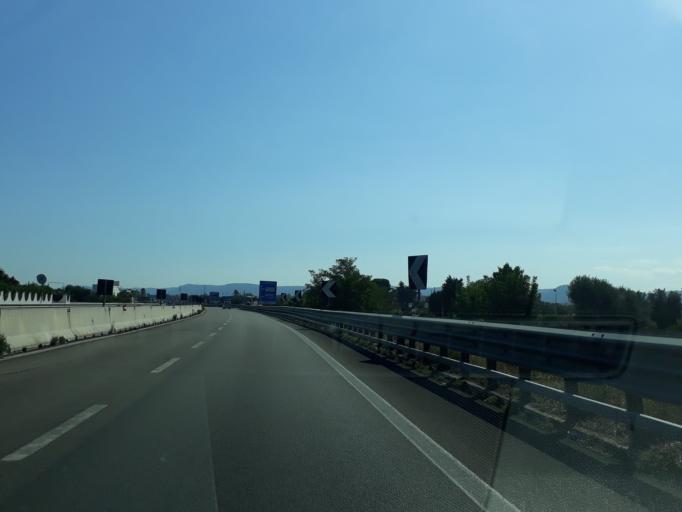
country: IT
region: Apulia
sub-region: Provincia di Brindisi
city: Fasano
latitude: 40.8582
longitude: 17.3498
